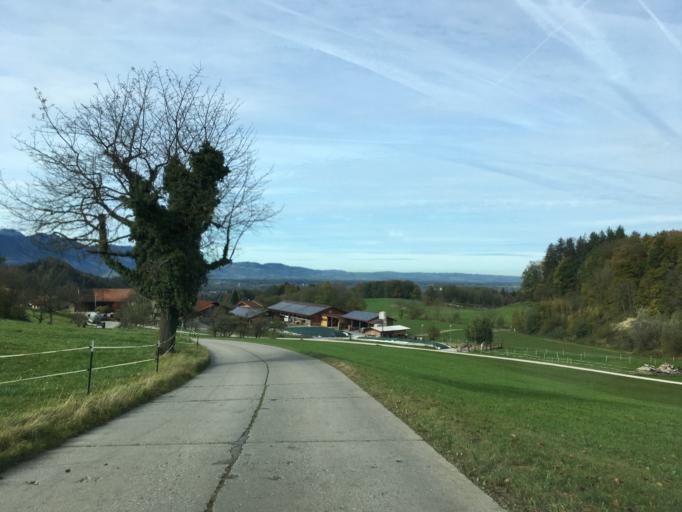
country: DE
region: Bavaria
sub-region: Upper Bavaria
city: Samerberg
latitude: 47.7851
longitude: 12.1850
